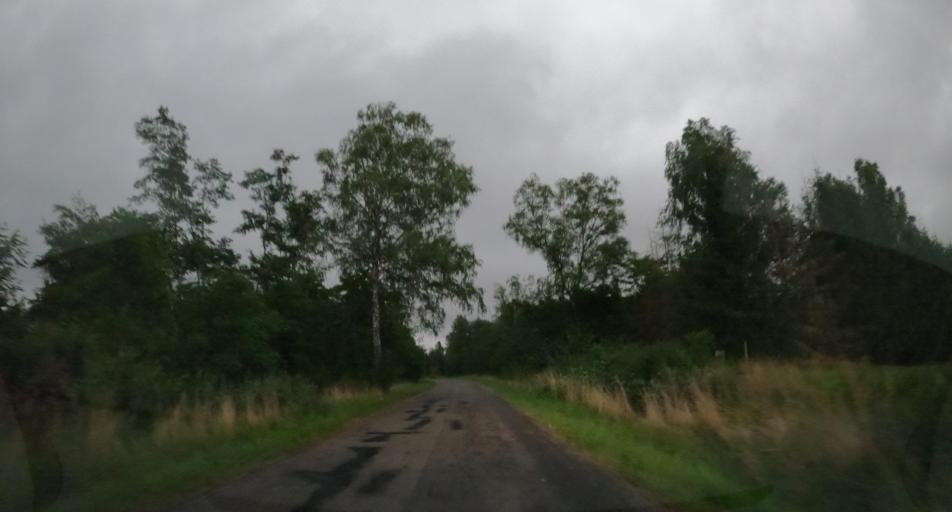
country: PL
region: West Pomeranian Voivodeship
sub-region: Powiat lobeski
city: Resko
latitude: 53.7588
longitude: 15.4120
